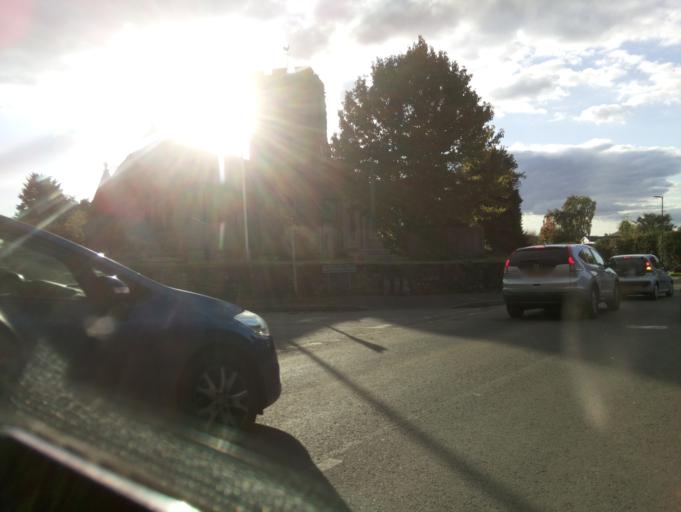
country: GB
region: England
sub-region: Herefordshire
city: Withington
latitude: 52.0662
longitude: -2.6561
